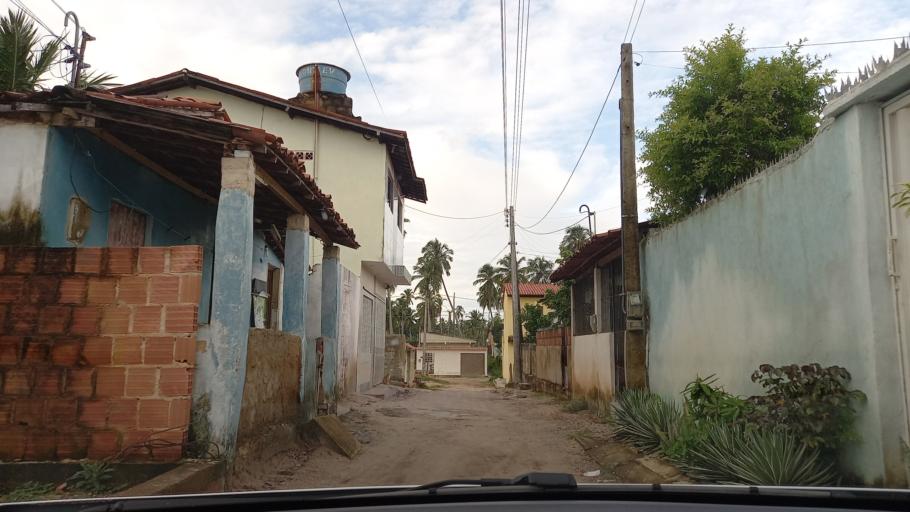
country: BR
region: Pernambuco
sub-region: Sao Jose Da Coroa Grande
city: Sao Jose da Coroa Grande
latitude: -8.9199
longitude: -35.1660
